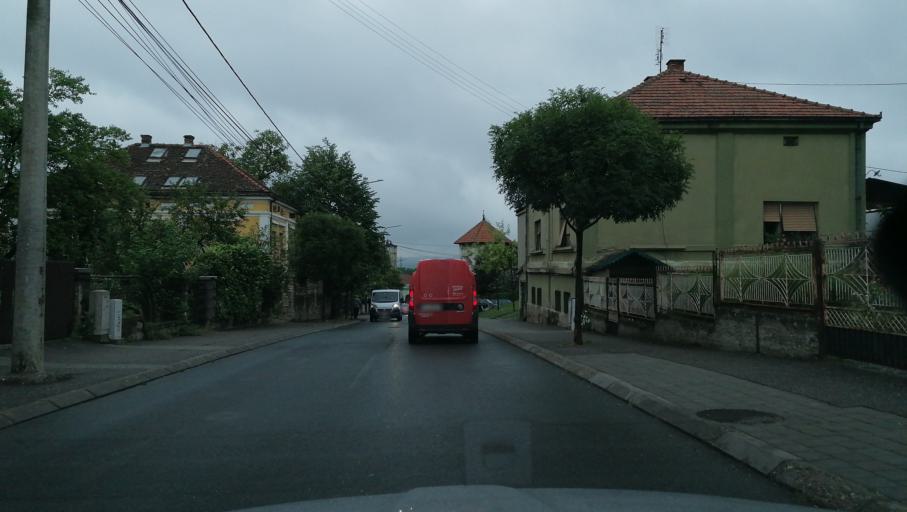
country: RS
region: Central Serbia
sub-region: Rasinski Okrug
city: Krusevac
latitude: 43.5830
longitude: 21.3202
